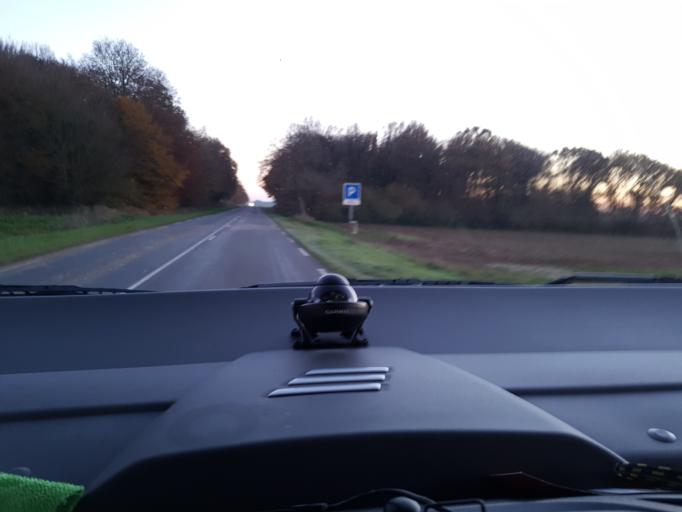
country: FR
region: Picardie
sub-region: Departement de la Somme
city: Rue
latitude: 50.2958
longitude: 1.7450
